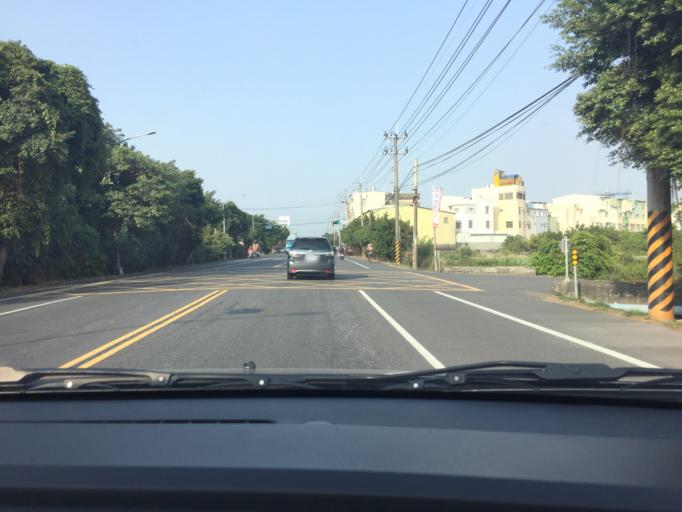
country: TW
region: Taiwan
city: Xinying
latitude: 23.1934
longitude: 120.2830
